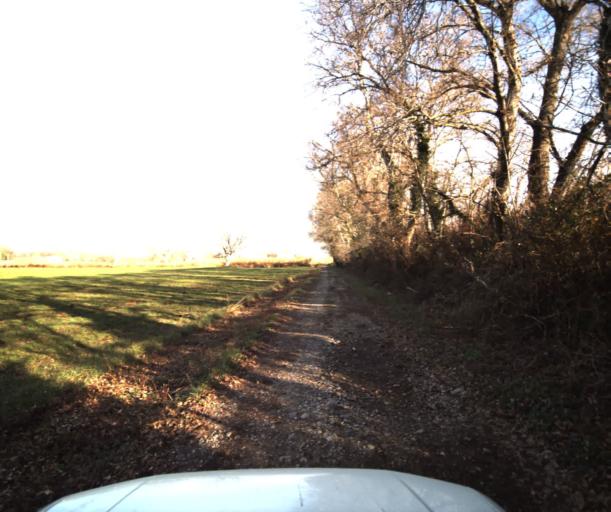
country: FR
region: Provence-Alpes-Cote d'Azur
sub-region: Departement du Vaucluse
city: Pertuis
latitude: 43.6722
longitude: 5.4835
